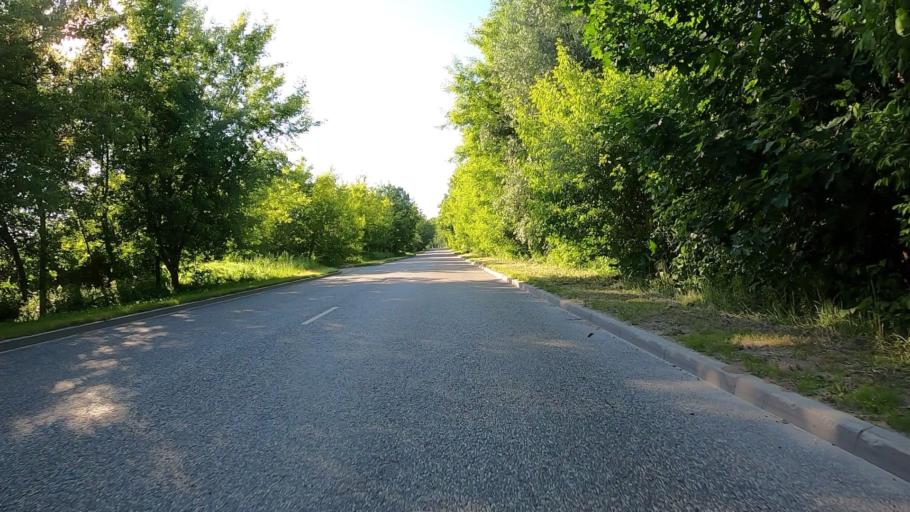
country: LV
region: Kekava
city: Kekava
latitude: 56.8891
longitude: 24.2473
